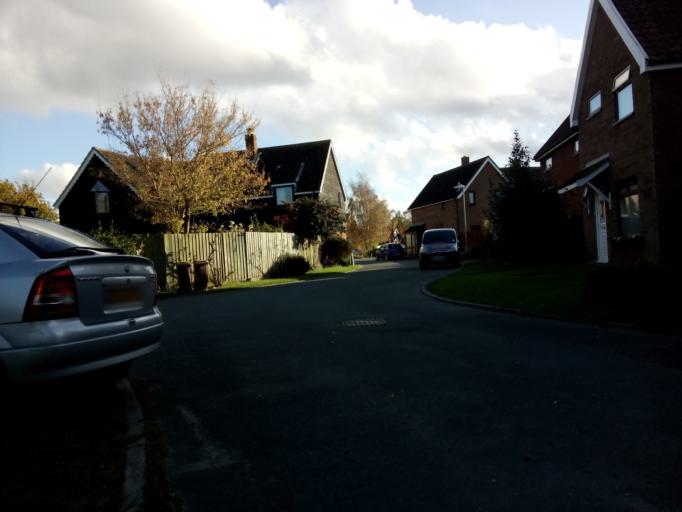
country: GB
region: England
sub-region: Suffolk
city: Kesgrave
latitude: 52.0650
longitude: 1.2739
